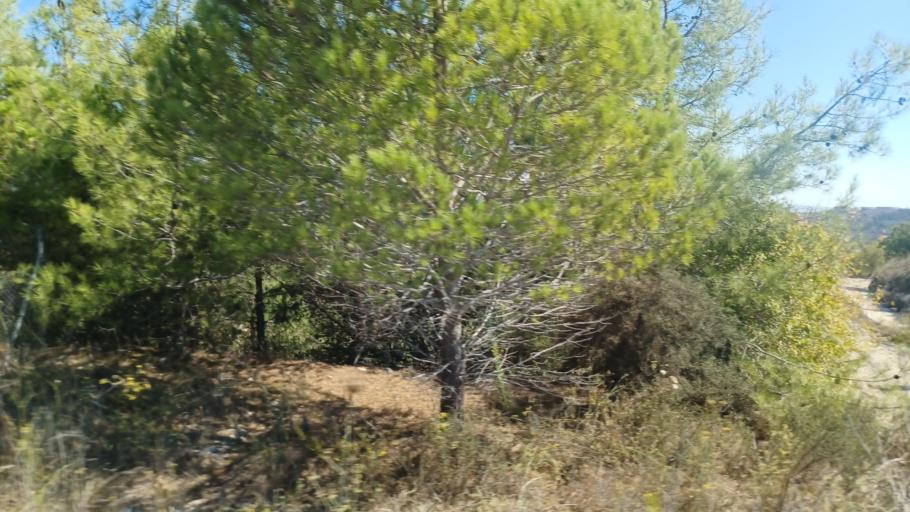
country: CY
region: Pafos
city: Mesogi
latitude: 34.8196
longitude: 32.4821
